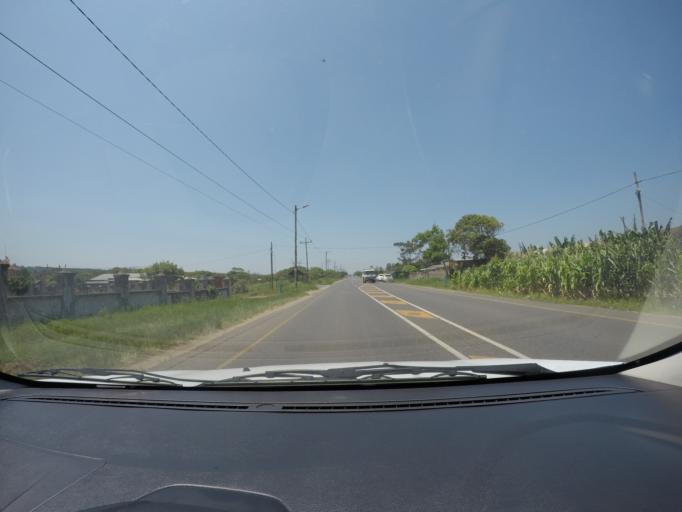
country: ZA
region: KwaZulu-Natal
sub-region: uThungulu District Municipality
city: eSikhawini
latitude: -28.8793
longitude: 31.8918
